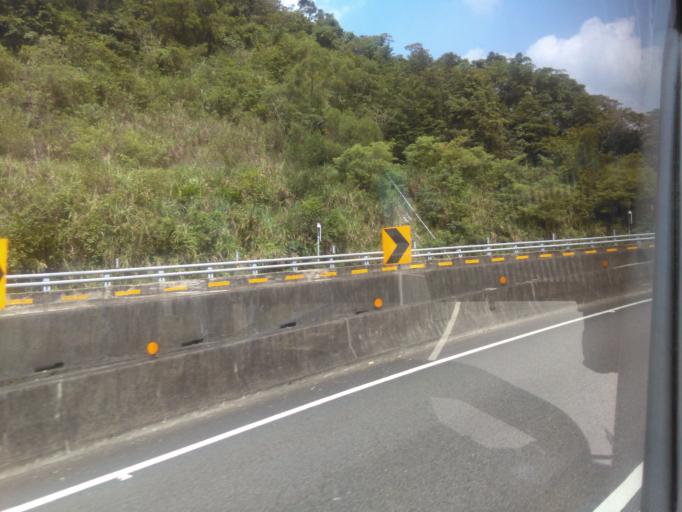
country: TW
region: Taipei
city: Taipei
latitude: 25.0361
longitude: 121.6190
